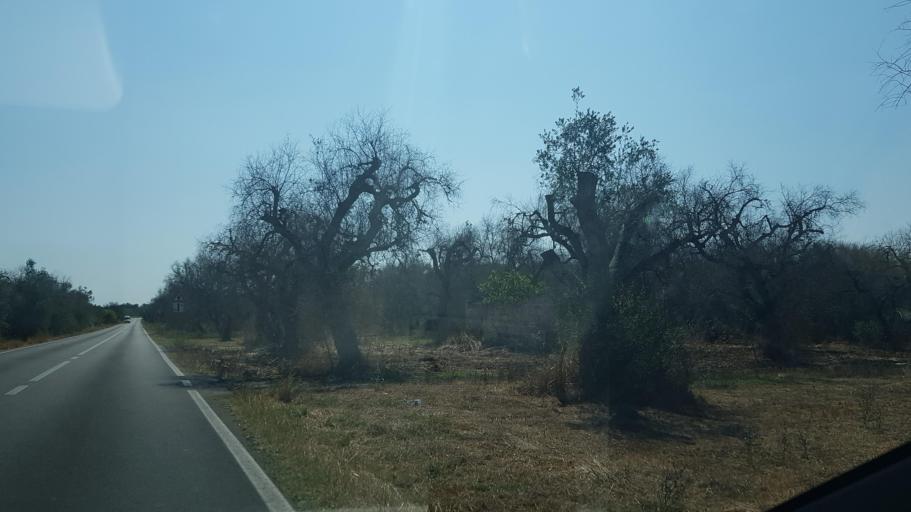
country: IT
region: Apulia
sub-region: Provincia di Lecce
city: Ruffano
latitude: 40.0031
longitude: 18.2881
